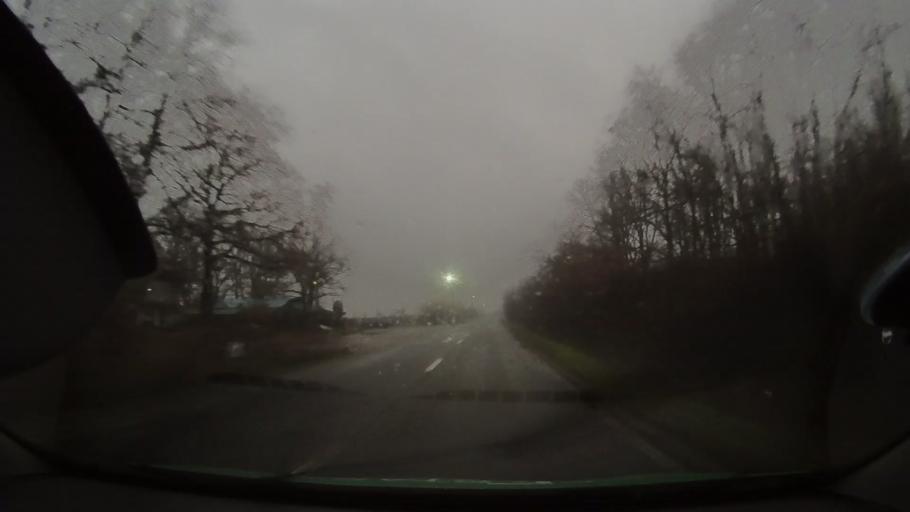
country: RO
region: Arad
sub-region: Comuna Beliu
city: Beliu
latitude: 46.5014
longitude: 21.9735
